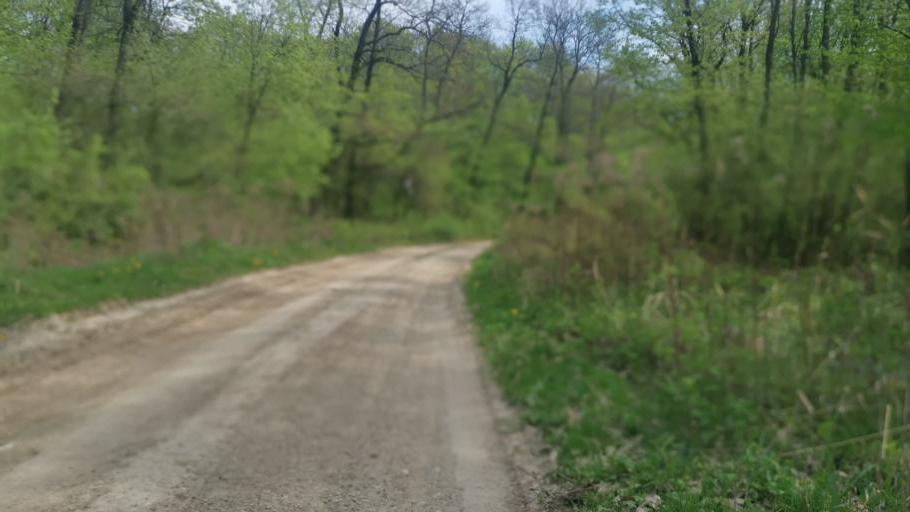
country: SK
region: Trnavsky
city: Smolenice
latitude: 48.5518
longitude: 17.4409
